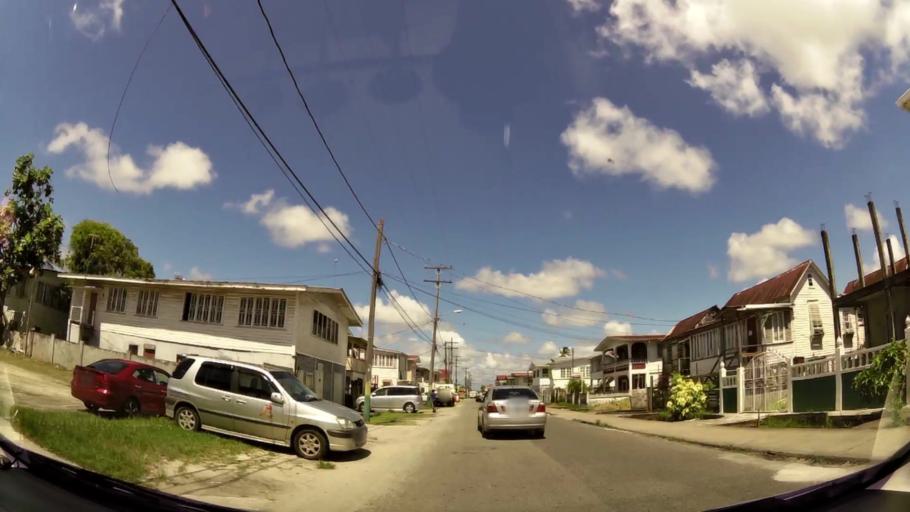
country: GY
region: Demerara-Mahaica
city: Georgetown
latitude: 6.8039
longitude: -58.1564
